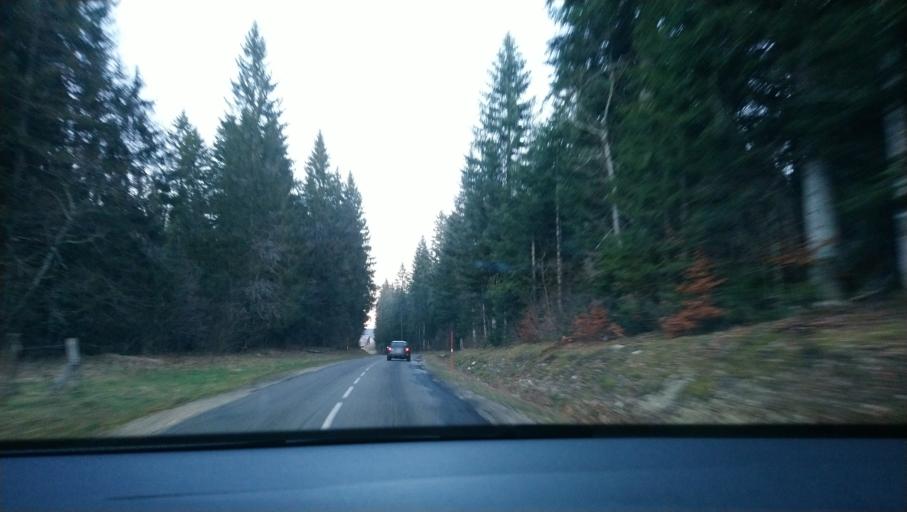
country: FR
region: Franche-Comte
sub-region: Departement du Doubs
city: Pontarlier
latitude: 46.8183
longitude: 6.2852
